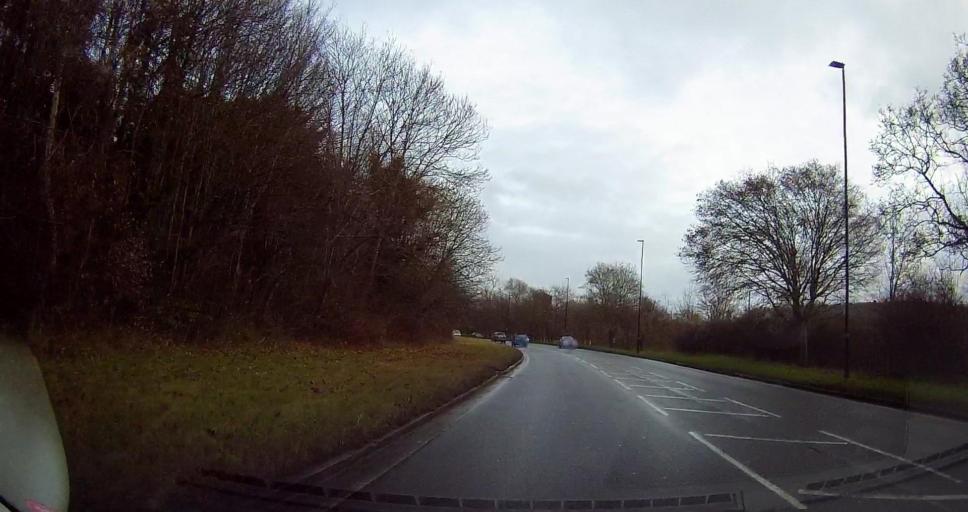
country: GB
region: England
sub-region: Greater London
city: Orpington
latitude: 51.3449
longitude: 0.0991
